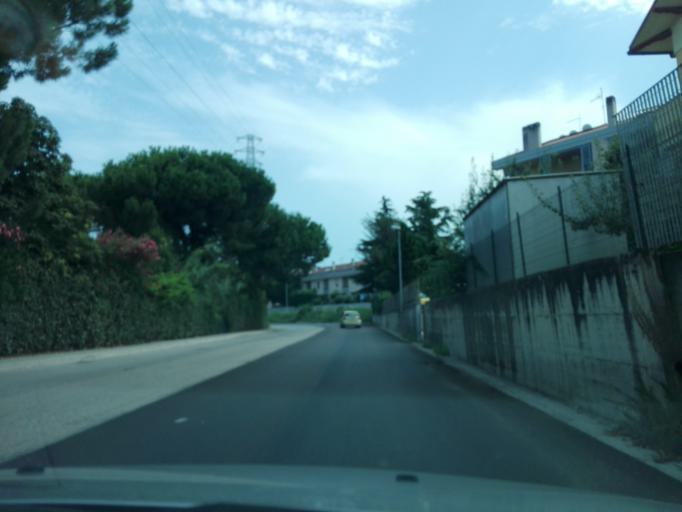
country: IT
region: Abruzzo
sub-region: Provincia di Pescara
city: Montesilvano Marina
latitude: 42.5041
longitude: 14.1332
